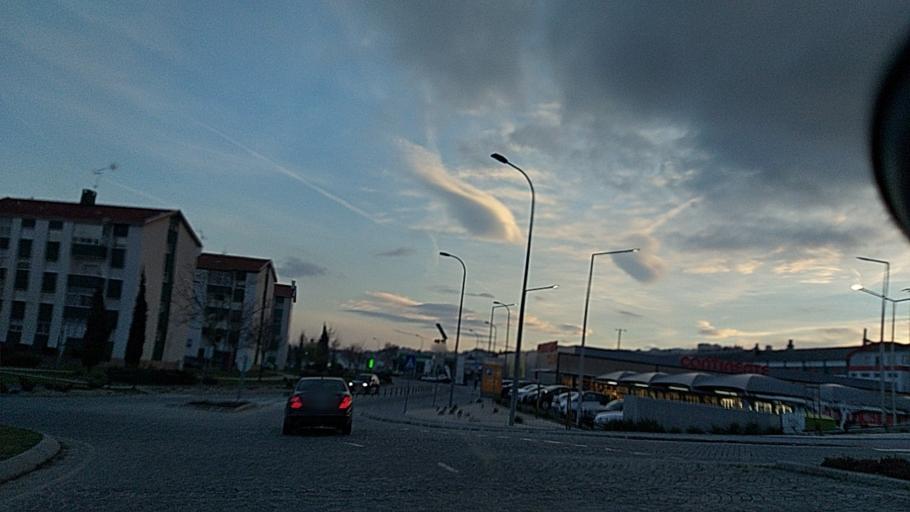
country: PT
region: Guarda
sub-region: Guarda
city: Sequeira
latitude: 40.5550
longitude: -7.2459
